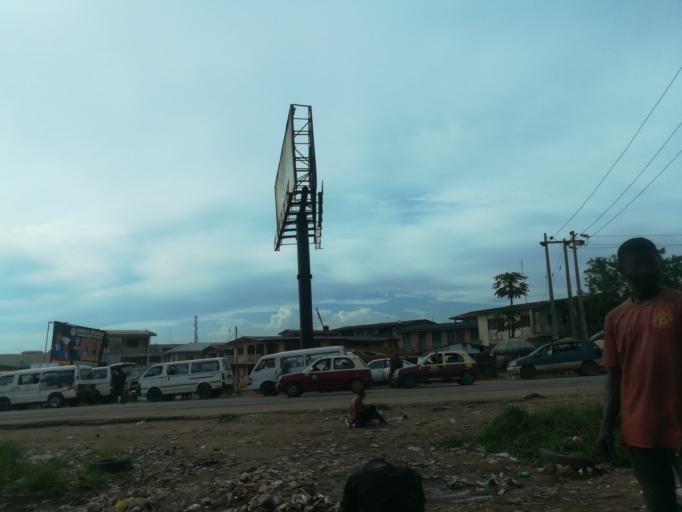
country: NG
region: Oyo
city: Ibadan
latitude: 7.4018
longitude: 3.9419
